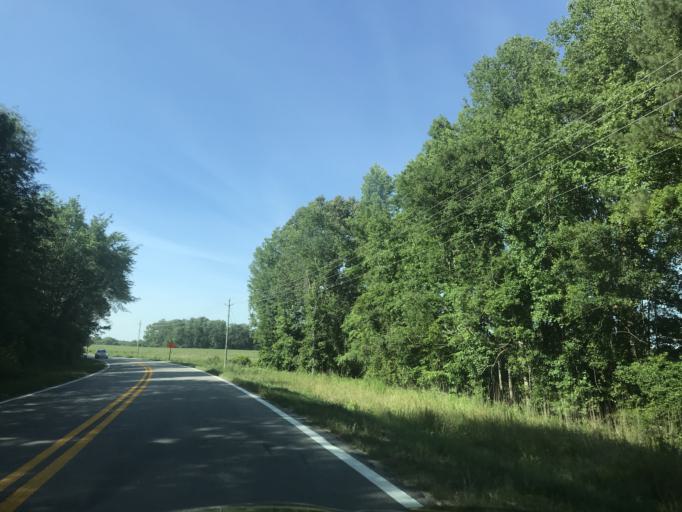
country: US
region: North Carolina
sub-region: Johnston County
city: Clayton
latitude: 35.6046
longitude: -78.5338
